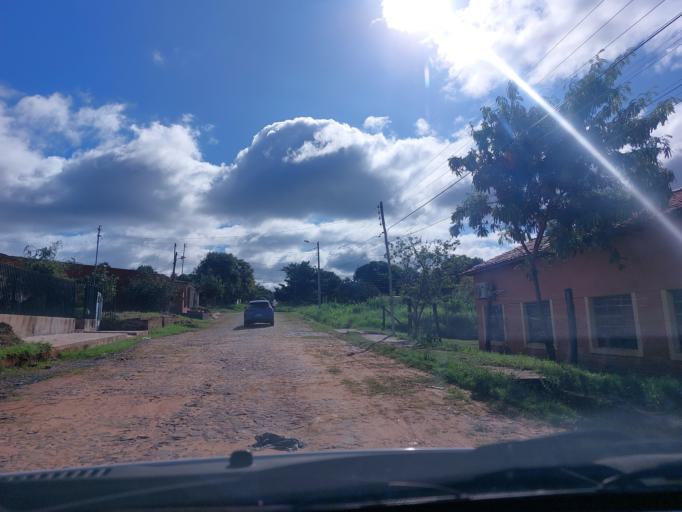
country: PY
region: San Pedro
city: Guayaybi
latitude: -24.6687
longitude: -56.4364
